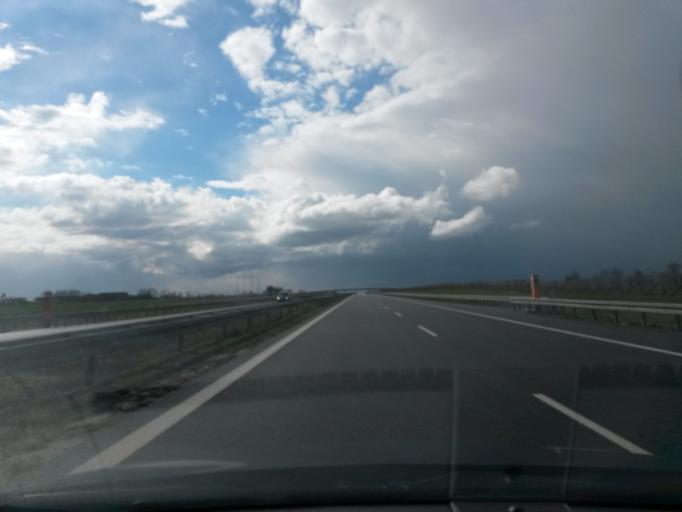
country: PL
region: Greater Poland Voivodeship
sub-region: Powiat wrzesinski
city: Nekla
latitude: 52.3185
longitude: 17.4803
